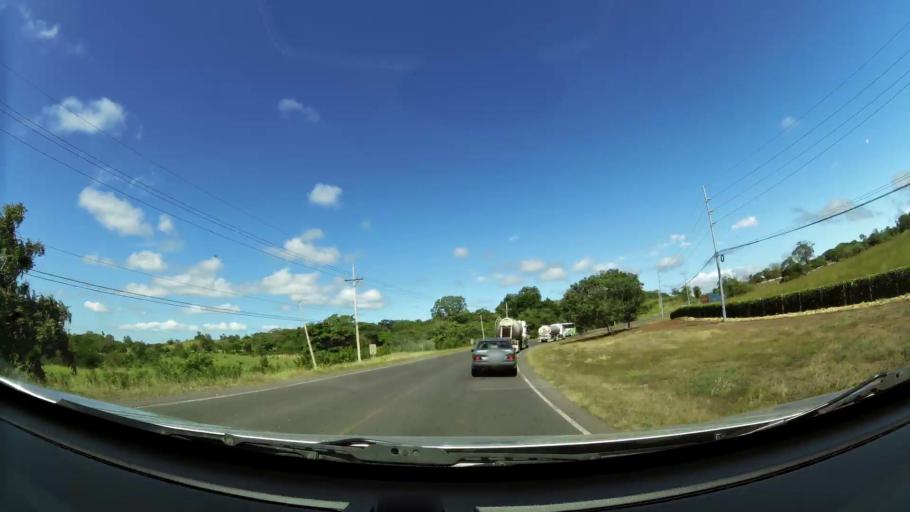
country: CR
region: Guanacaste
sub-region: Canton de Canas
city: Canas
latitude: 10.4054
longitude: -85.0864
